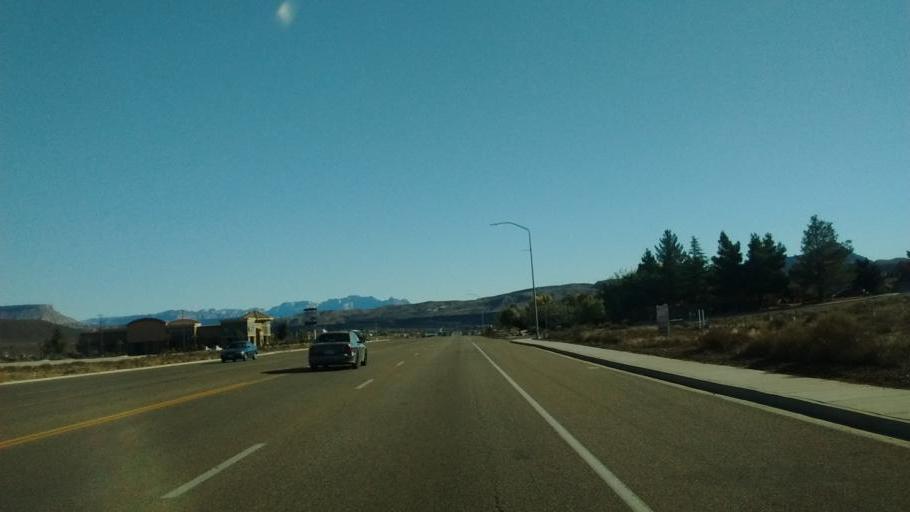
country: US
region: Utah
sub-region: Washington County
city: Hurricane
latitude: 37.1762
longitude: -113.3285
